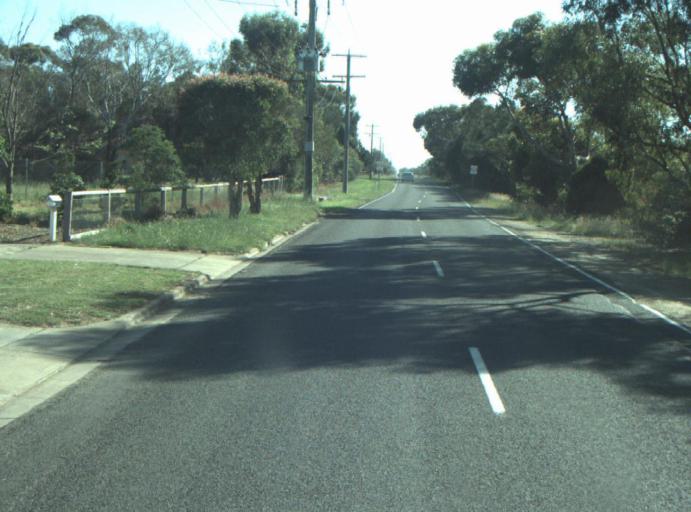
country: AU
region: Victoria
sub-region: Greater Geelong
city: Lara
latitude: -38.0171
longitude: 144.4190
